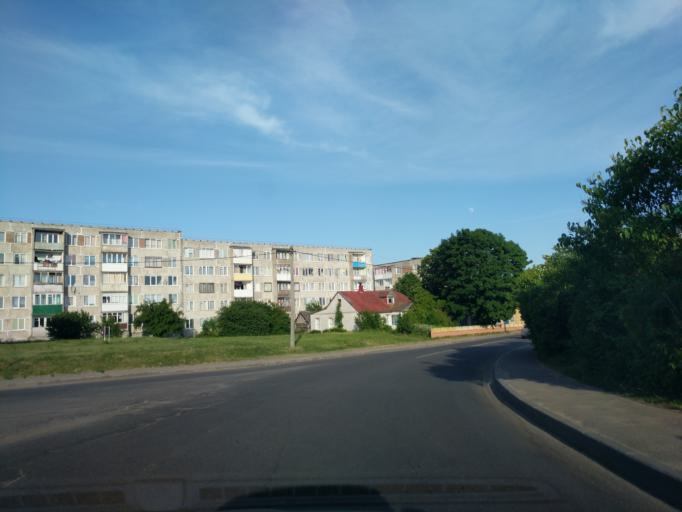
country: BY
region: Grodnenskaya
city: Ashmyany
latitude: 54.4255
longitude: 25.9280
